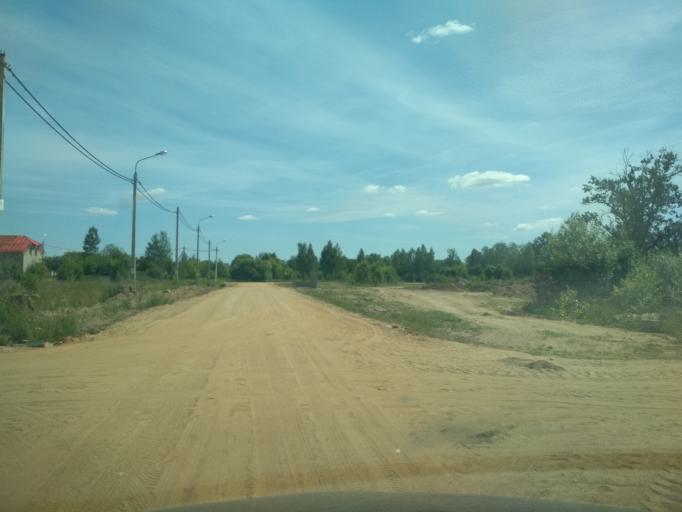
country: BY
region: Minsk
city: Mar''ina Horka
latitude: 53.5101
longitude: 28.1624
